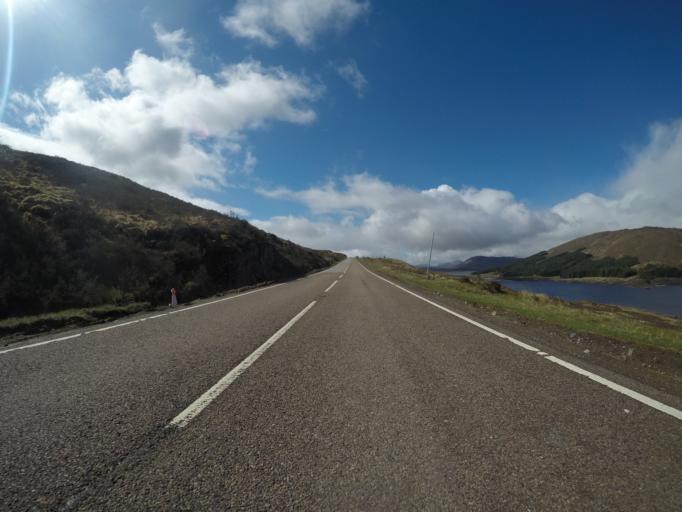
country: GB
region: Scotland
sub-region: Highland
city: Spean Bridge
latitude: 57.1178
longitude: -4.9800
